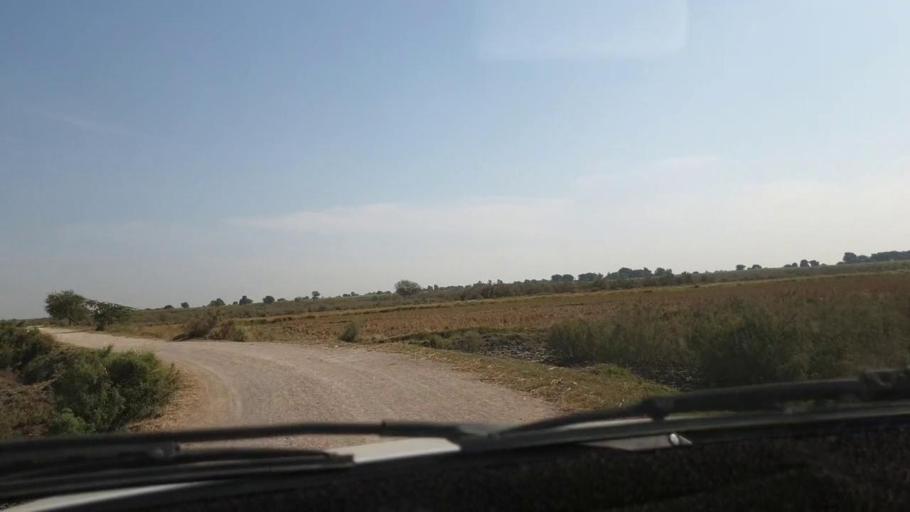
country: PK
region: Sindh
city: Bulri
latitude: 24.9510
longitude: 68.4225
